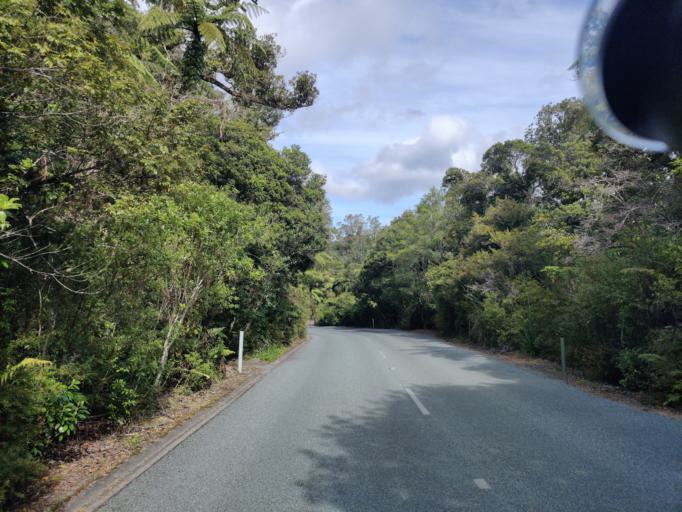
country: NZ
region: Northland
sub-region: Kaipara District
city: Dargaville
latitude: -35.6387
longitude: 173.5593
